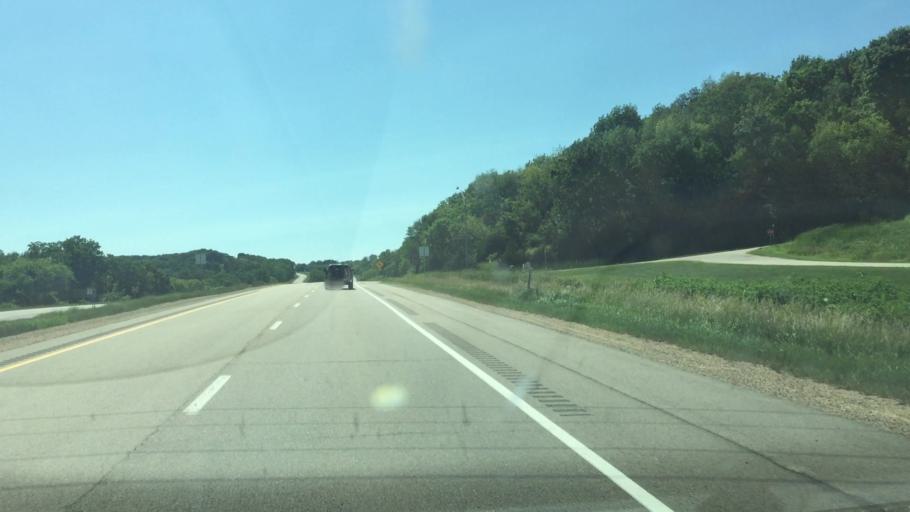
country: US
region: Iowa
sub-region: Dubuque County
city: Dubuque
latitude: 42.4189
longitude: -90.7021
